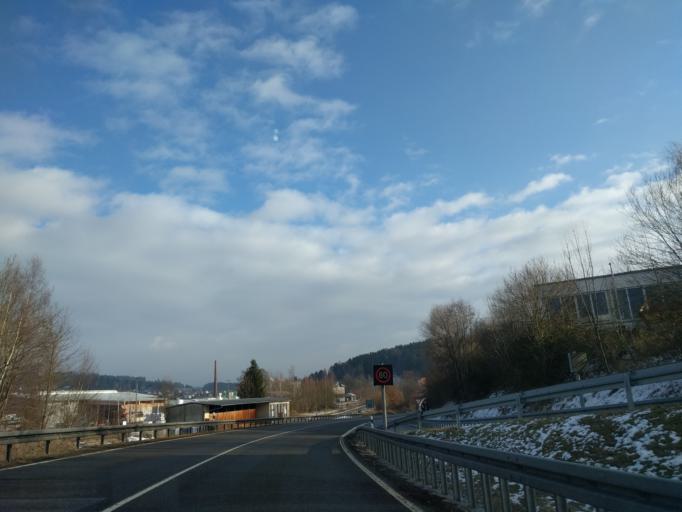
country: DE
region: Bavaria
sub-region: Lower Bavaria
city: Regen
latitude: 48.9667
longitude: 13.1330
